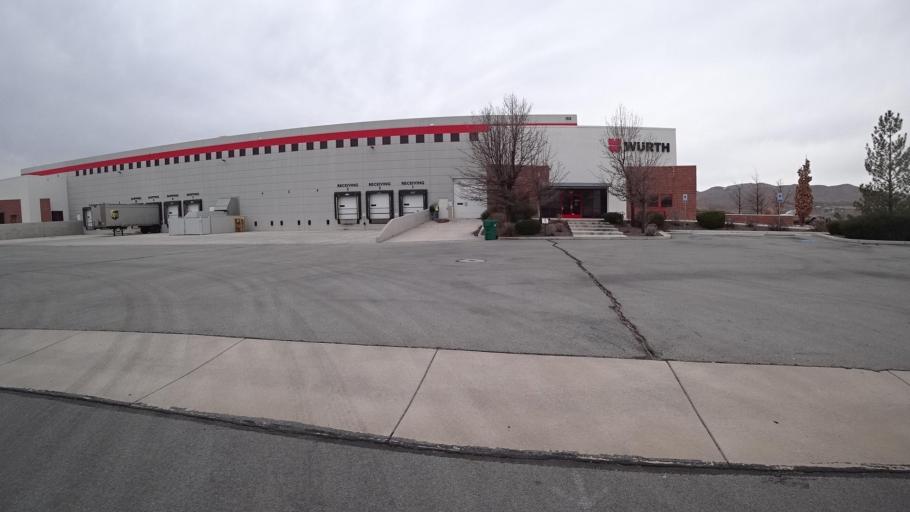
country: US
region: Nevada
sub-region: Washoe County
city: Spanish Springs
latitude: 39.6727
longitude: -119.7087
